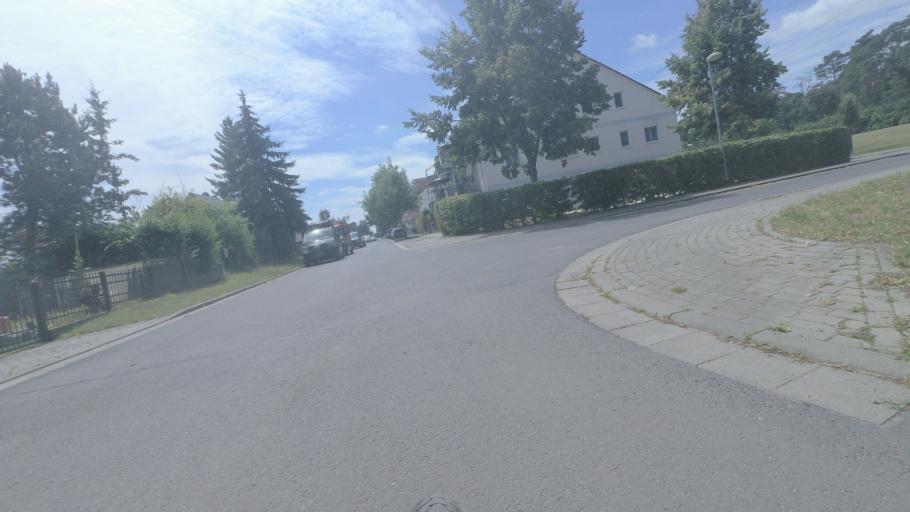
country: DE
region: Berlin
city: Lichtenrade
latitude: 52.3634
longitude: 13.4337
